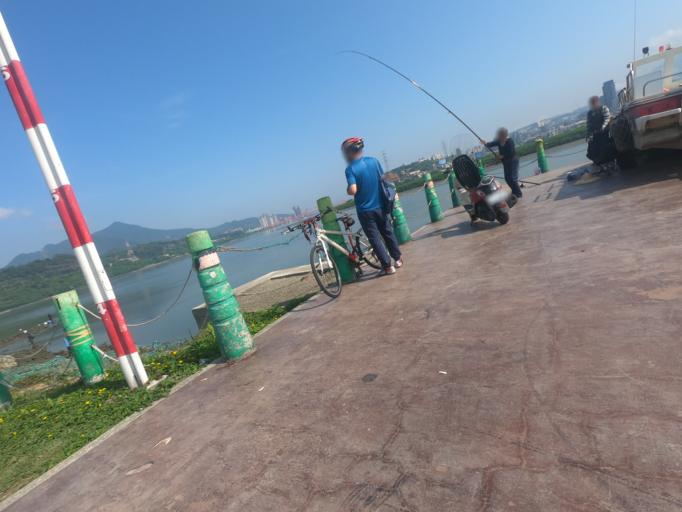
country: TW
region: Taipei
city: Taipei
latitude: 25.1104
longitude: 121.4656
